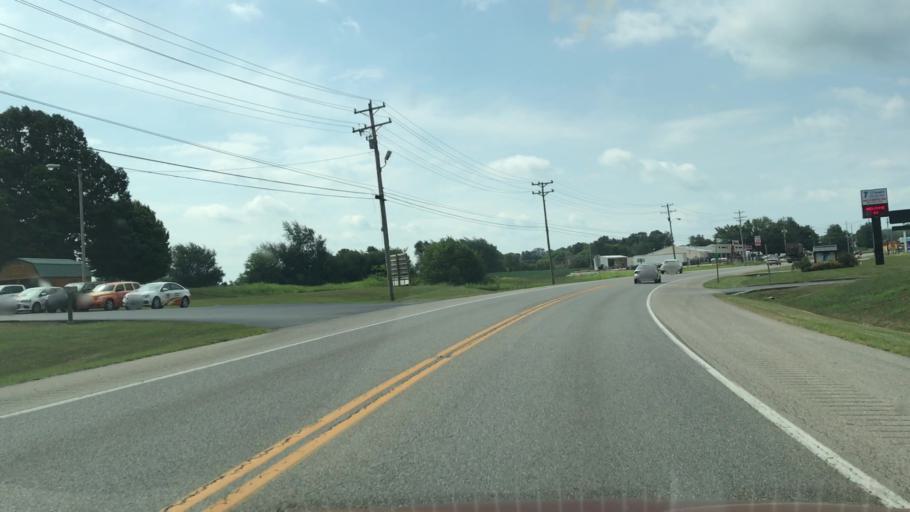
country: US
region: Kentucky
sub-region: Barren County
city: Cave City
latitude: 37.1263
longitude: -85.9615
